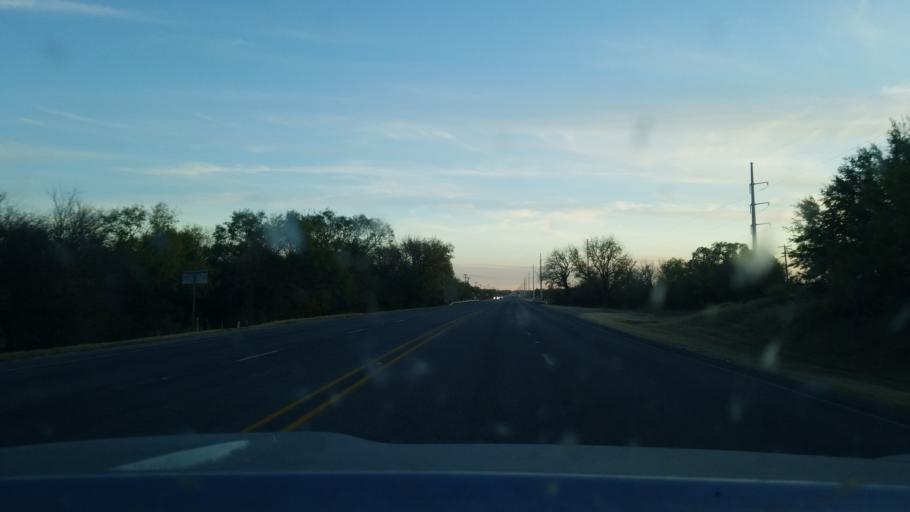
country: US
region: Texas
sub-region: Stephens County
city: Breckenridge
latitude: 32.7421
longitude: -98.9026
